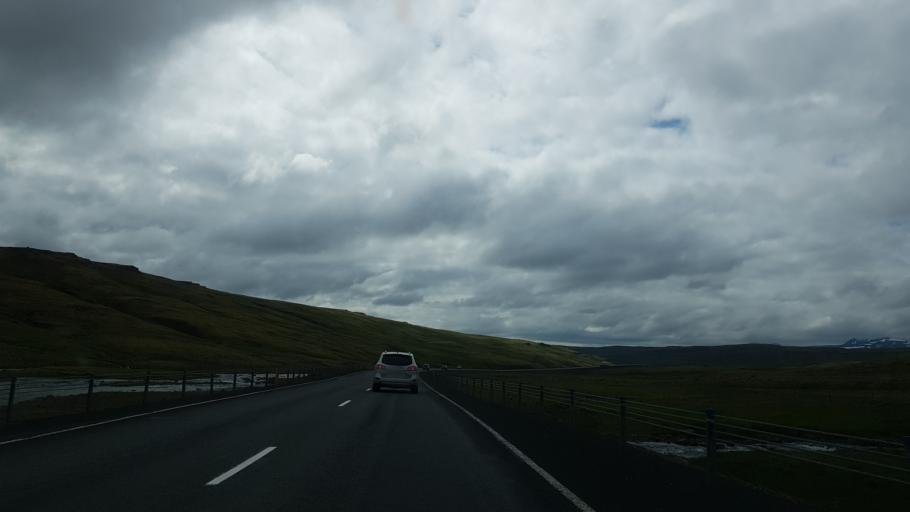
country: IS
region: West
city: Borgarnes
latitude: 64.9148
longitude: -21.1415
